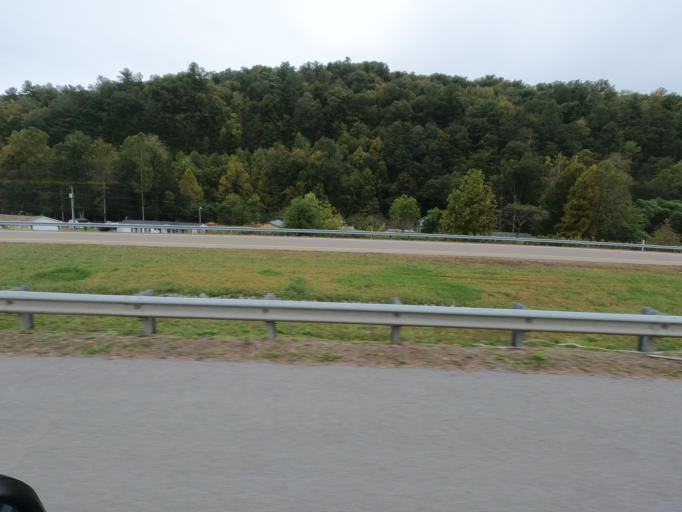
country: US
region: Tennessee
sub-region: Unicoi County
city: Unicoi
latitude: 36.1866
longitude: -82.3781
